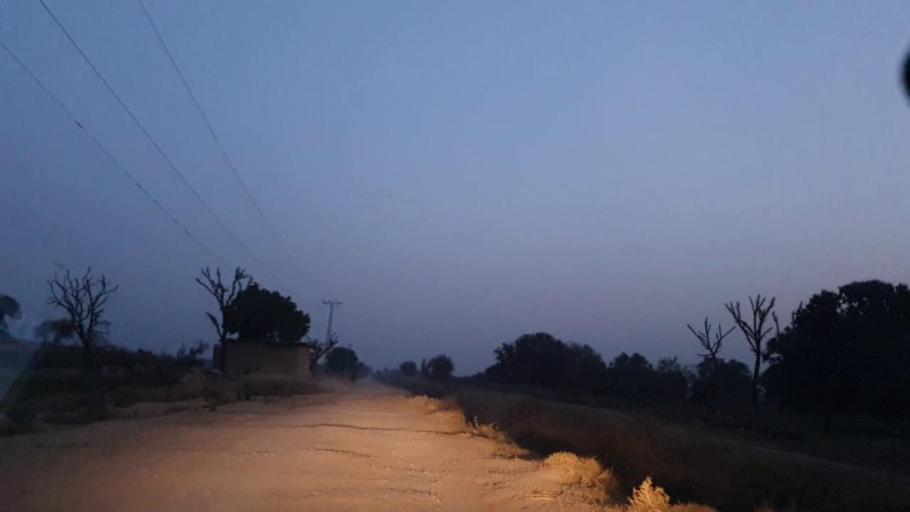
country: PK
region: Sindh
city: Tando Ghulam Ali
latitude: 25.1011
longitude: 68.9116
